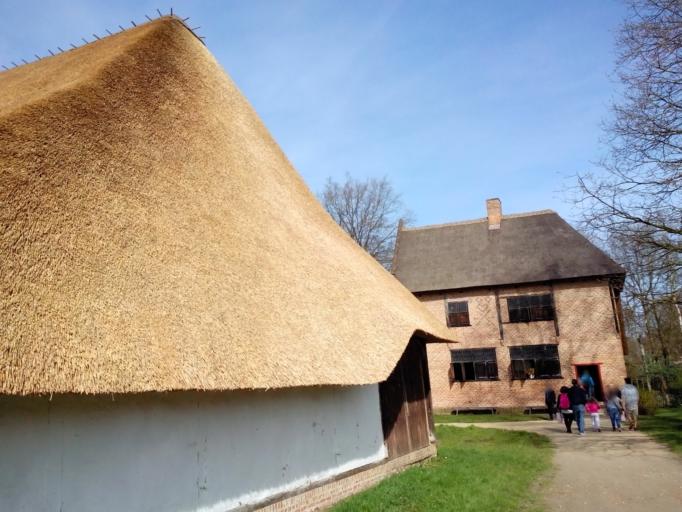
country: BE
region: Flanders
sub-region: Provincie Limburg
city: Zonhoven
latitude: 50.9652
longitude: 5.4050
